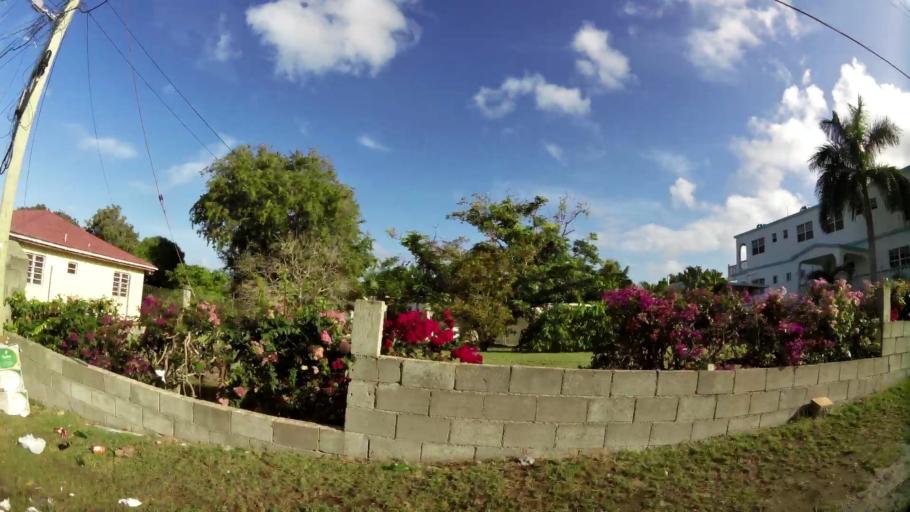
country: KN
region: Saint Paul Charlestown
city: Charlestown
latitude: 17.1450
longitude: -62.6256
